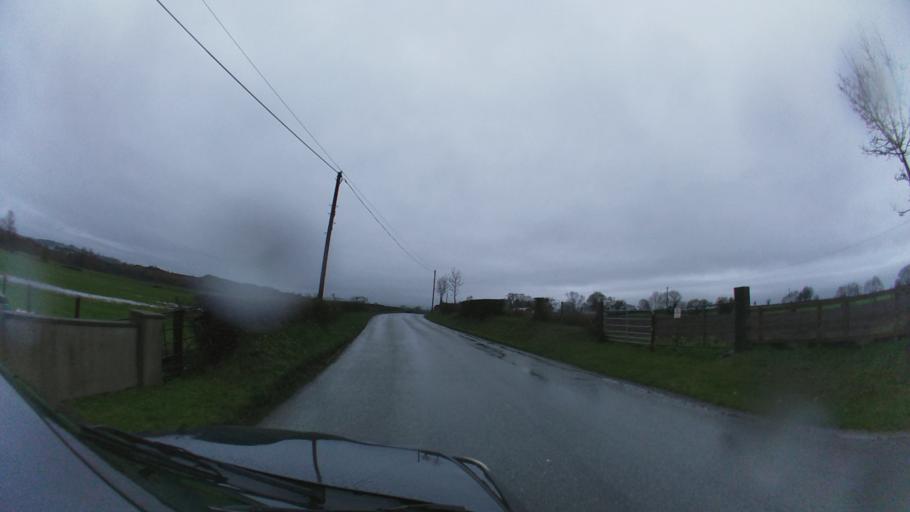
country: IE
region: Leinster
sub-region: County Carlow
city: Bagenalstown
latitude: 52.6452
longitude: -6.9900
